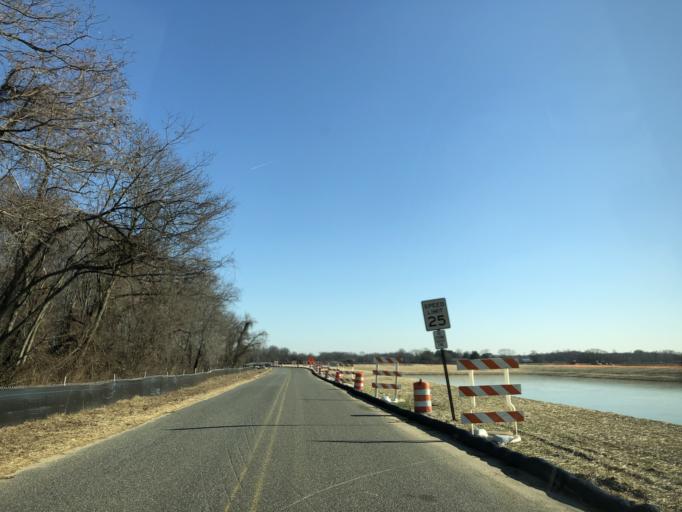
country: US
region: New Jersey
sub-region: Gloucester County
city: Beckett
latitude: 39.7933
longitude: -75.3515
